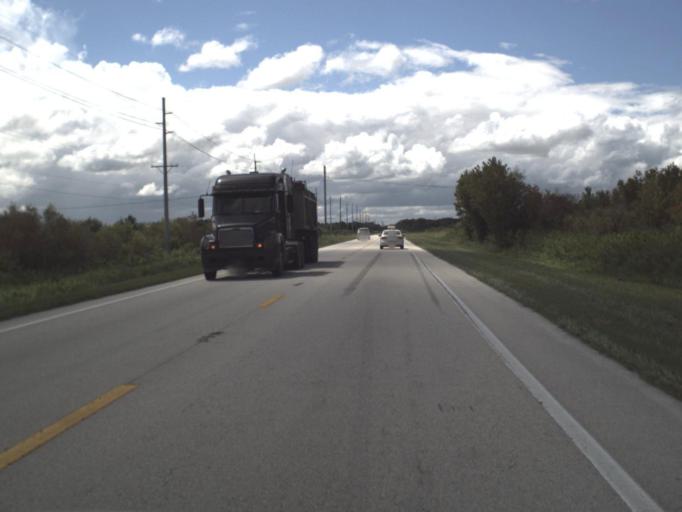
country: US
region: Florida
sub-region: Polk County
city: Mulberry
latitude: 27.8109
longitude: -81.9812
